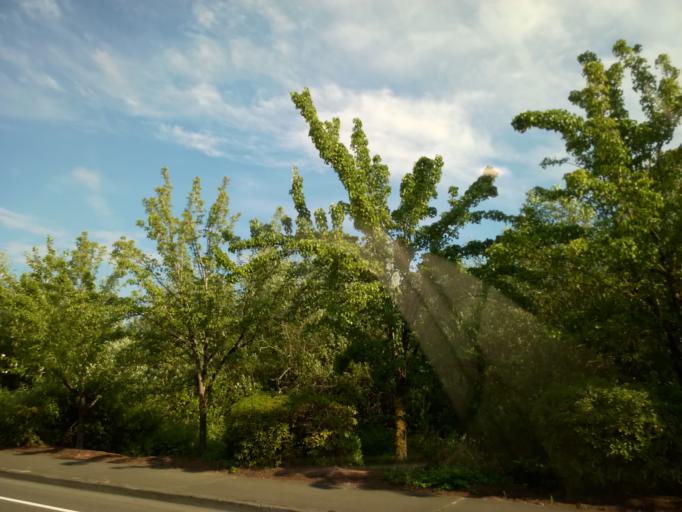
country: US
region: Washington
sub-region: King County
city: Bothell
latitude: 47.7786
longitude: -122.1845
